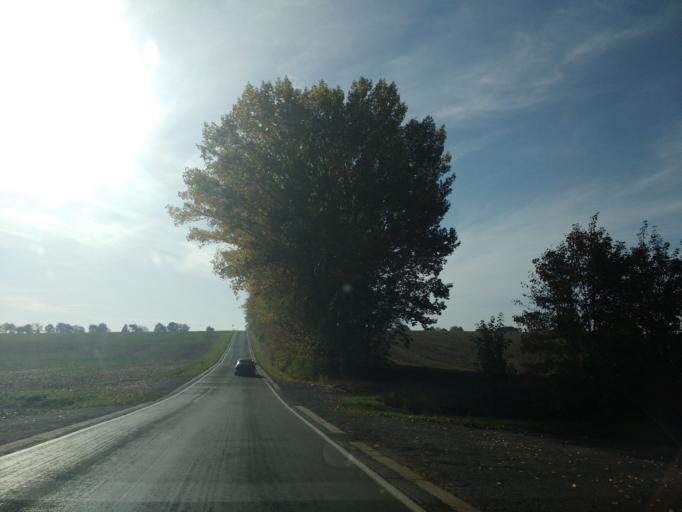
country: DE
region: Thuringia
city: Seebach
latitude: 51.1497
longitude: 10.5205
